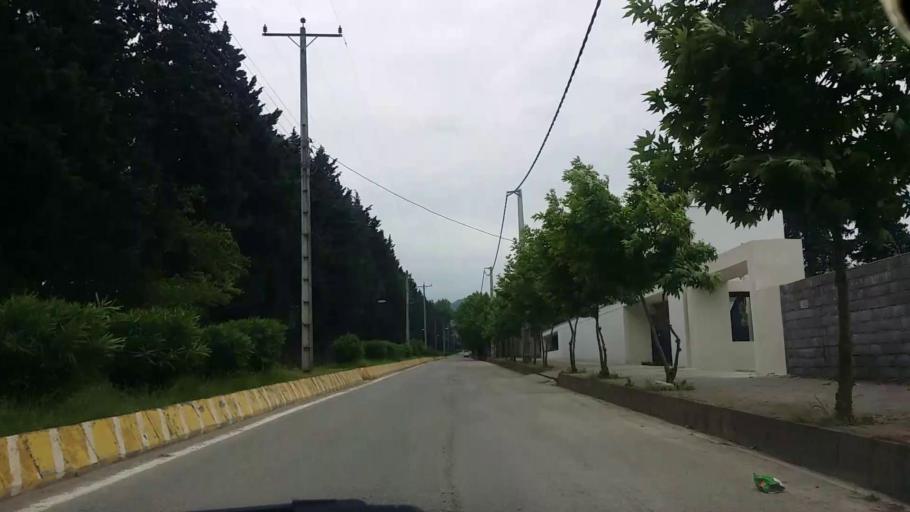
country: IR
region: Mazandaran
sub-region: Nowshahr
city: Nowshahr
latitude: 36.6352
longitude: 51.5025
